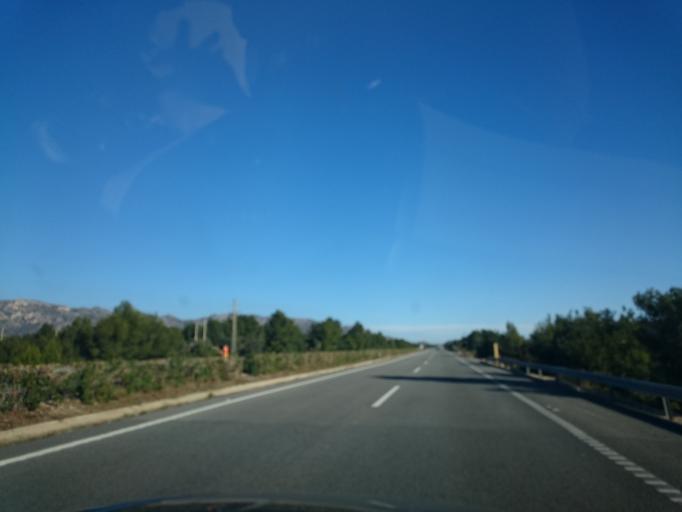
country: ES
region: Catalonia
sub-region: Provincia de Tarragona
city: l'Ametlla de Mar
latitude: 40.9140
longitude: 0.8265
